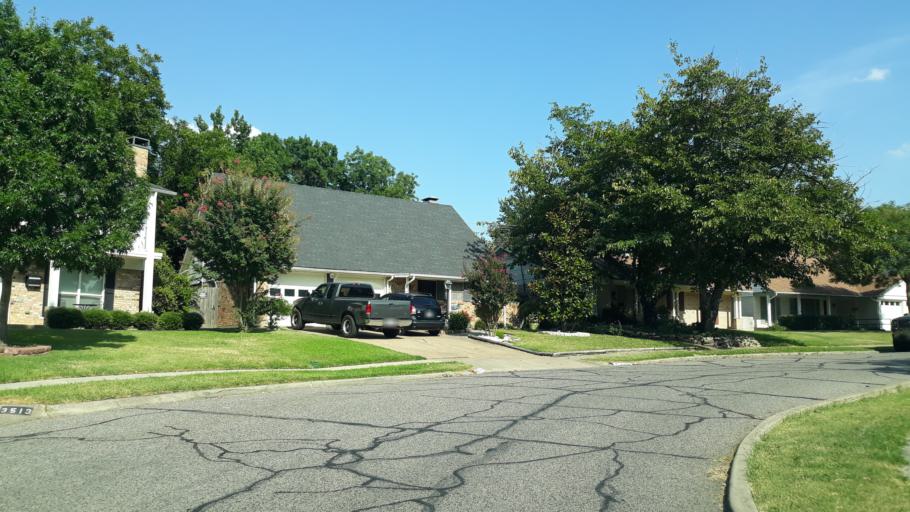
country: US
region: Texas
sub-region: Dallas County
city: Irving
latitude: 32.8442
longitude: -96.9962
